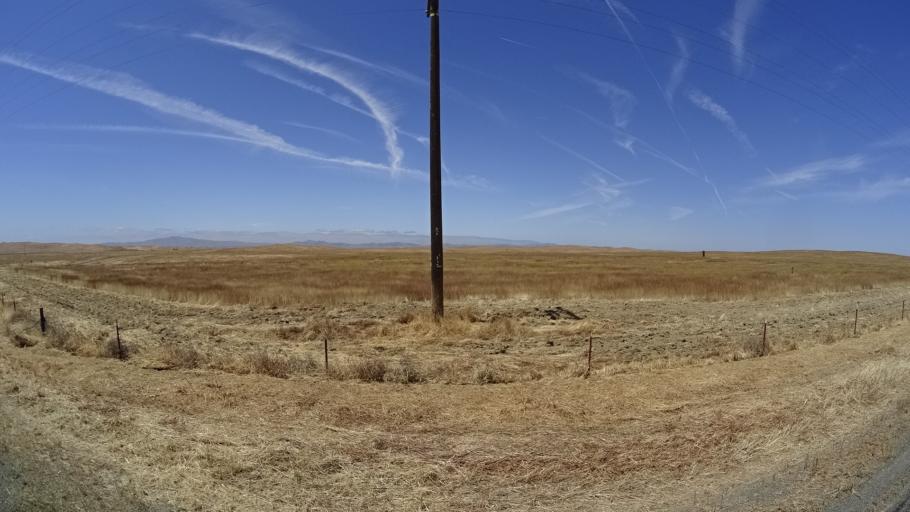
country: US
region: California
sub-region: Kings County
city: Kettleman City
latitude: 35.8507
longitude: -119.9153
